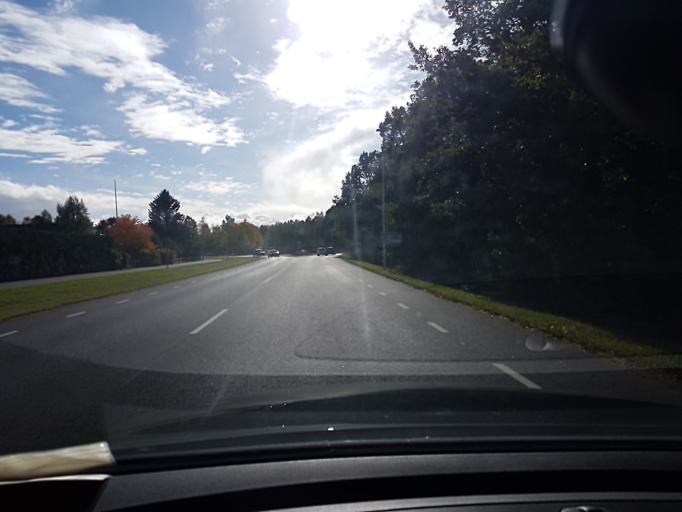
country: SE
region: Kronoberg
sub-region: Vaxjo Kommun
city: Vaexjoe
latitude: 56.8563
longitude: 14.8073
